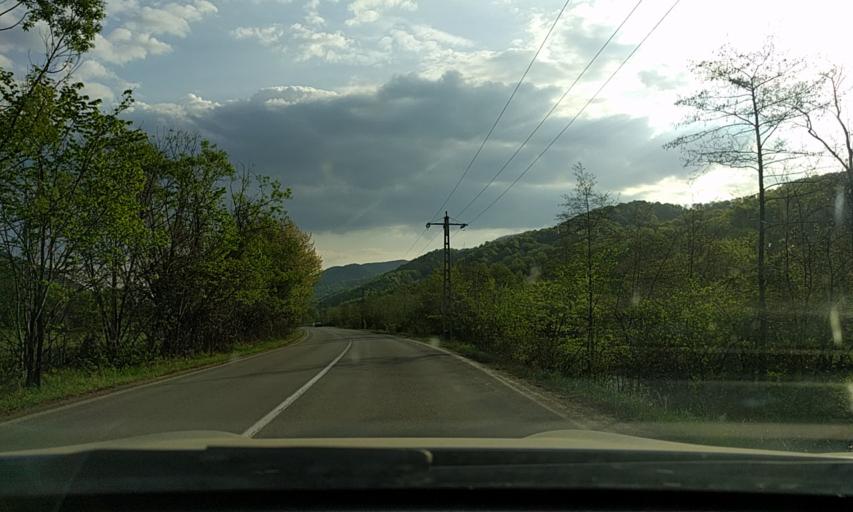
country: RO
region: Bacau
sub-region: Oras Slanic-Moldova
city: Slanic-Moldova
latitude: 46.1270
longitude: 26.4390
